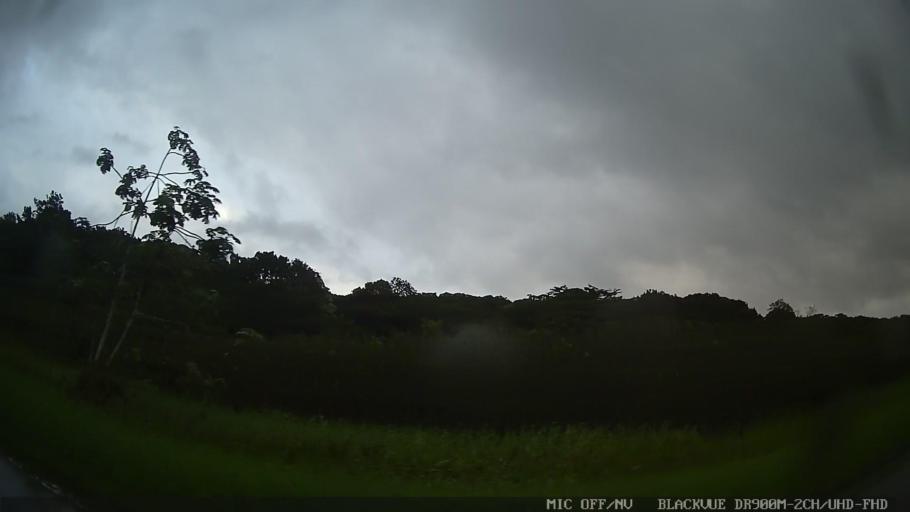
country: BR
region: Sao Paulo
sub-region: Itanhaem
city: Itanhaem
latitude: -24.2053
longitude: -46.8508
